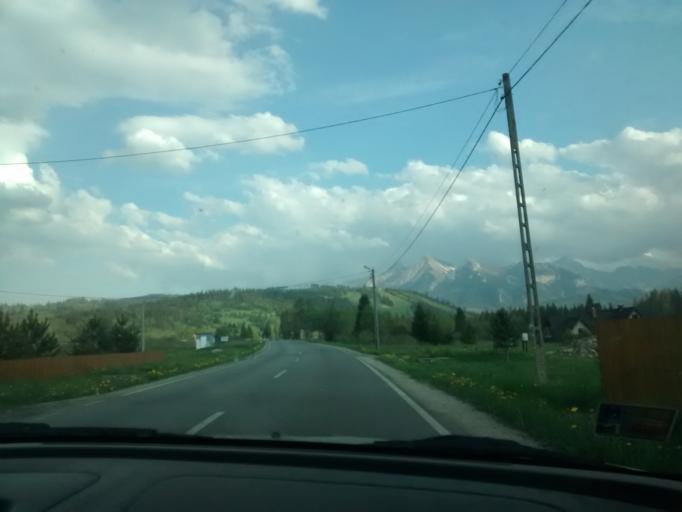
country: PL
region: Lesser Poland Voivodeship
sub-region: Powiat tatrzanski
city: Bukowina Tatrzanska
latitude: 49.3324
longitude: 20.1478
